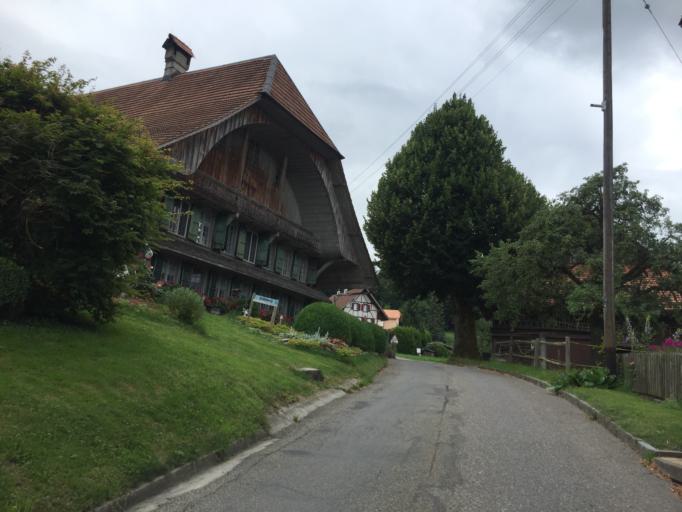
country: CH
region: Bern
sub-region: Bern-Mittelland District
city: Stettlen
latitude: 46.9512
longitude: 7.5194
